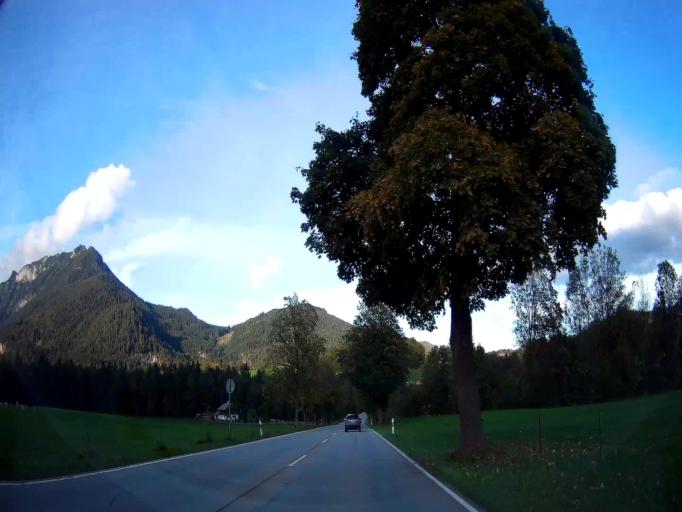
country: DE
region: Bavaria
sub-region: Upper Bavaria
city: Bischofswiesen
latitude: 47.6389
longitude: 12.9655
